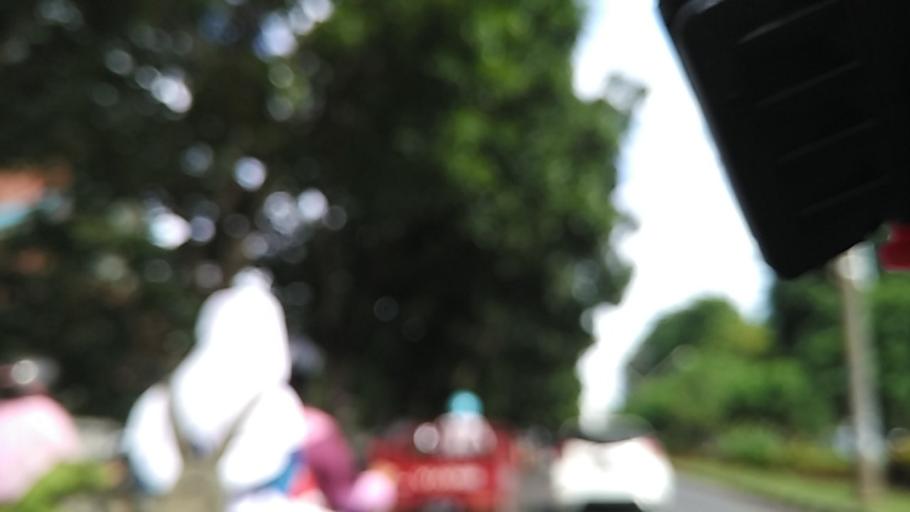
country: ID
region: Central Java
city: Semarang
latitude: -7.0541
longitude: 110.4327
